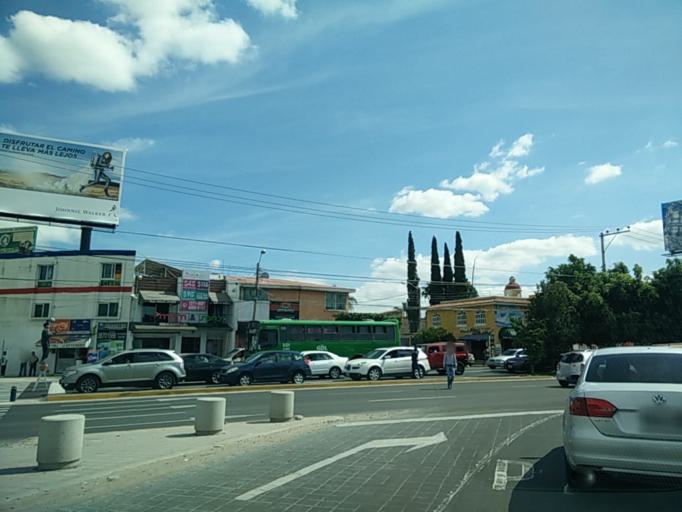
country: MX
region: Jalisco
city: Nuevo Mexico
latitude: 20.7297
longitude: -103.4312
